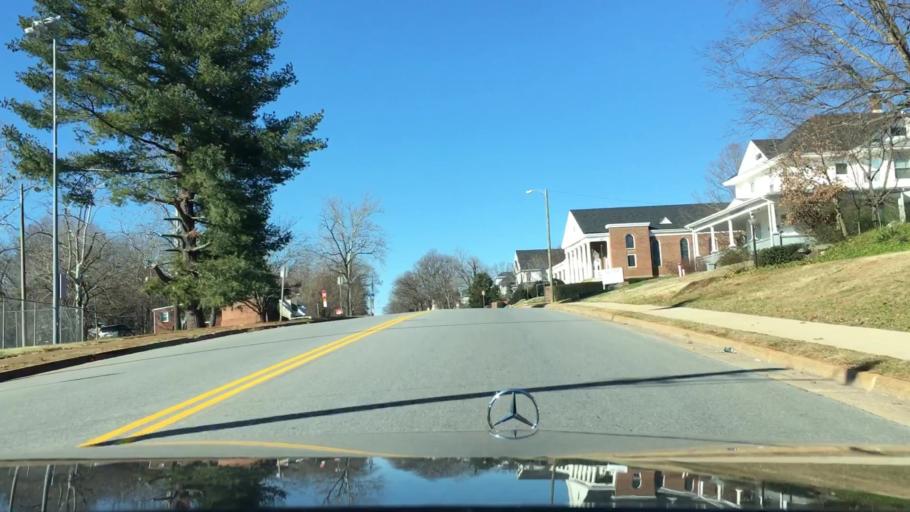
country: US
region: Virginia
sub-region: Campbell County
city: Altavista
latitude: 37.1104
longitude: -79.2946
